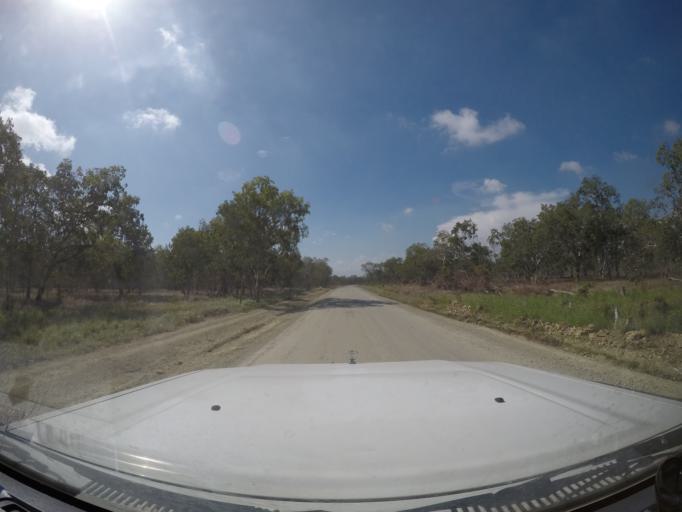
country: PG
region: Central Province
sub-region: Rigo
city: Kwikila
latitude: -9.9857
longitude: 147.6795
